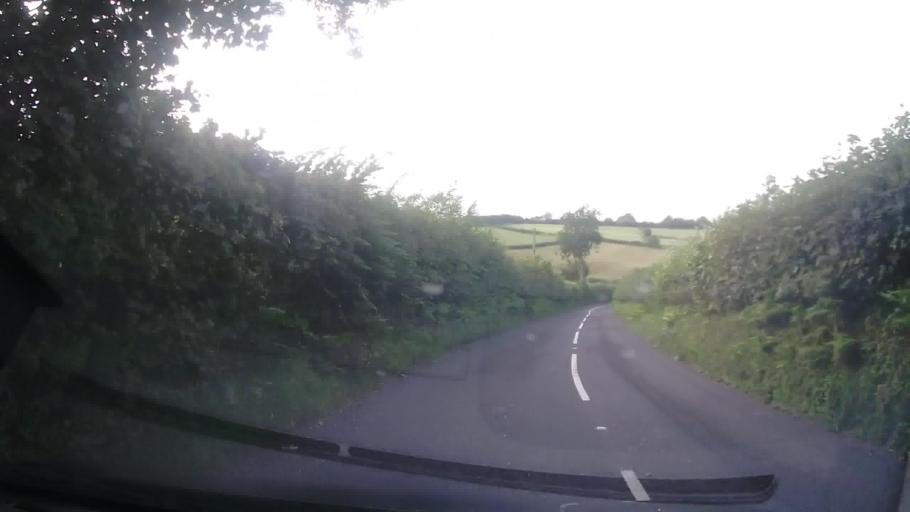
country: GB
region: England
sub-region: Shropshire
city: Acton
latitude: 52.4101
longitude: -3.0421
